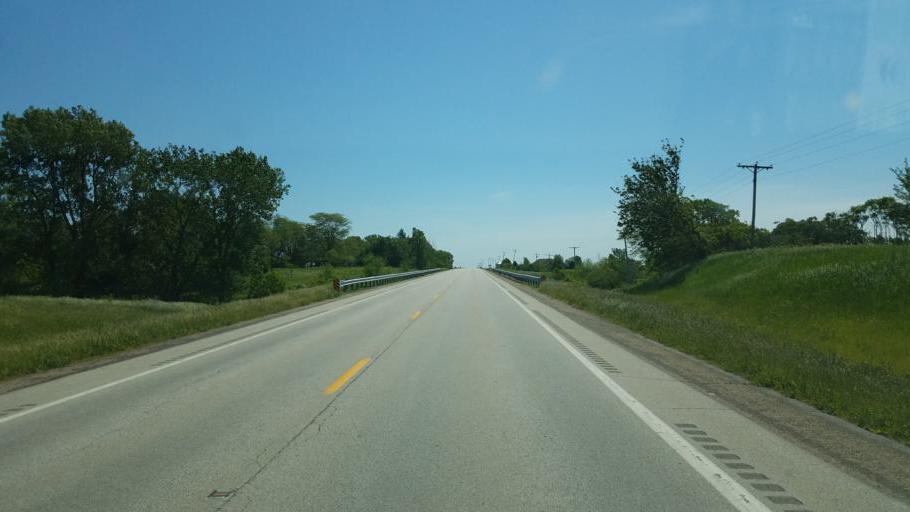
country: US
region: Illinois
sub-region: McLean County
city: Heyworth
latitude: 40.3122
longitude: -88.9529
